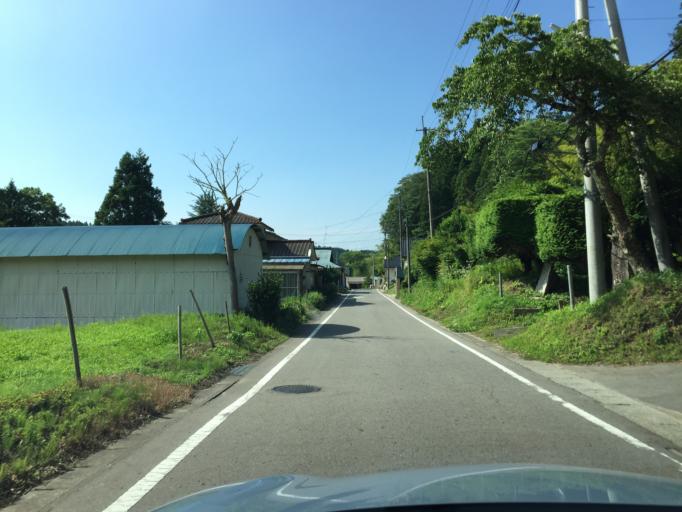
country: JP
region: Fukushima
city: Ishikawa
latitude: 37.1823
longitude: 140.6244
